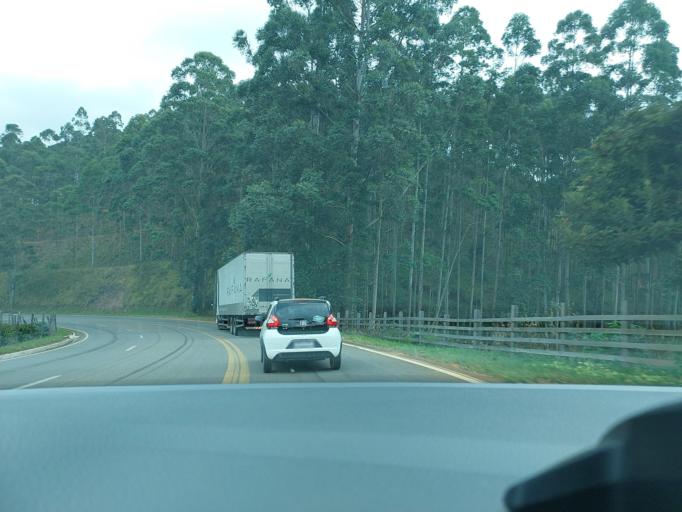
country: BR
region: Minas Gerais
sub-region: Mirai
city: Mirai
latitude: -20.9671
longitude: -42.5923
